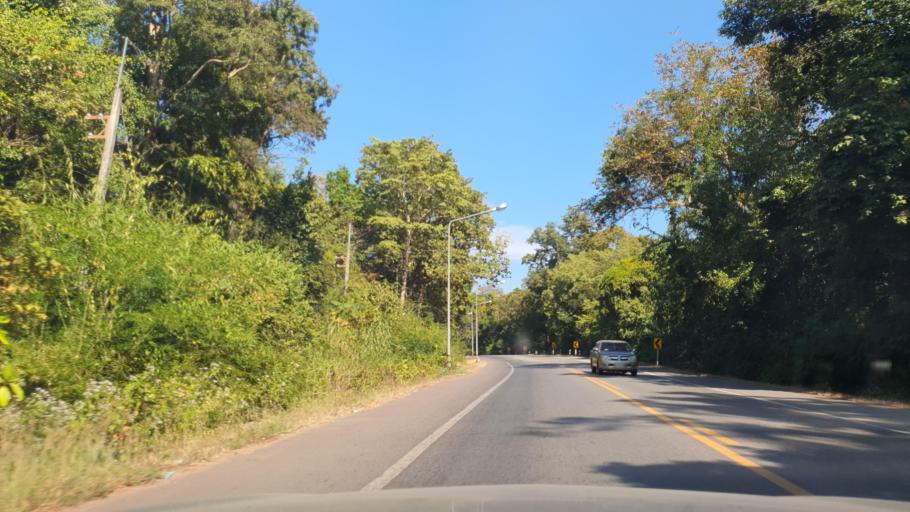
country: TH
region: Sakon Nakhon
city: Phu Phan
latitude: 17.1002
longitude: 103.9926
